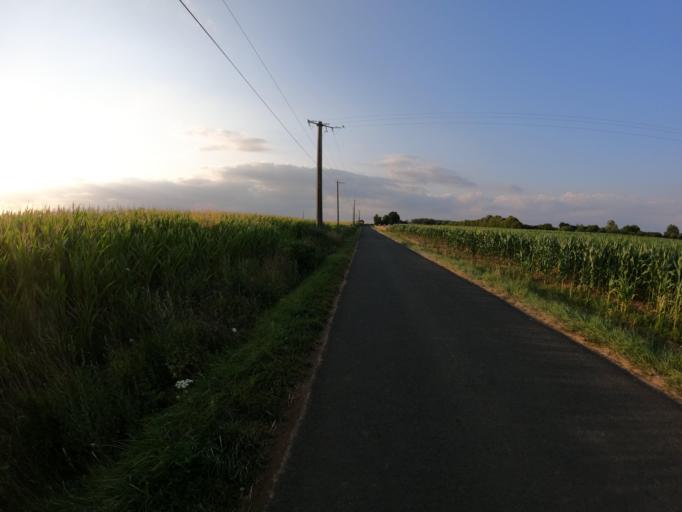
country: FR
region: Pays de la Loire
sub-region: Departement de la Sarthe
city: Brulon
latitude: 47.9268
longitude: -0.2295
